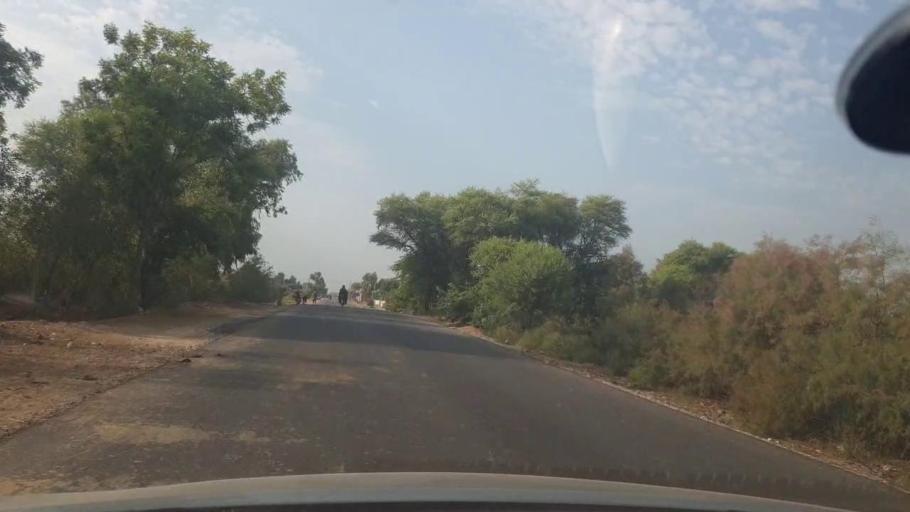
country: PK
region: Sindh
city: Jacobabad
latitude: 28.1112
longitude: 68.3266
